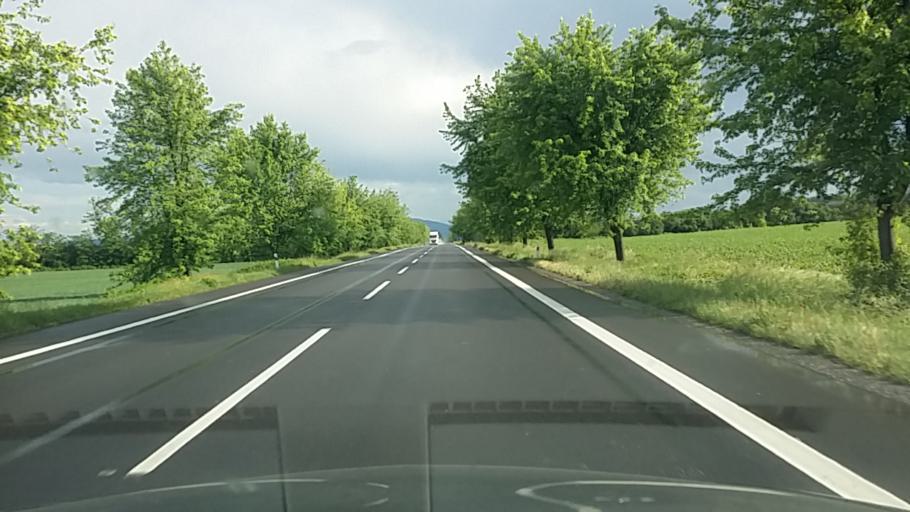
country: SK
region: Banskobystricky
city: Dudince
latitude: 48.1410
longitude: 18.8737
